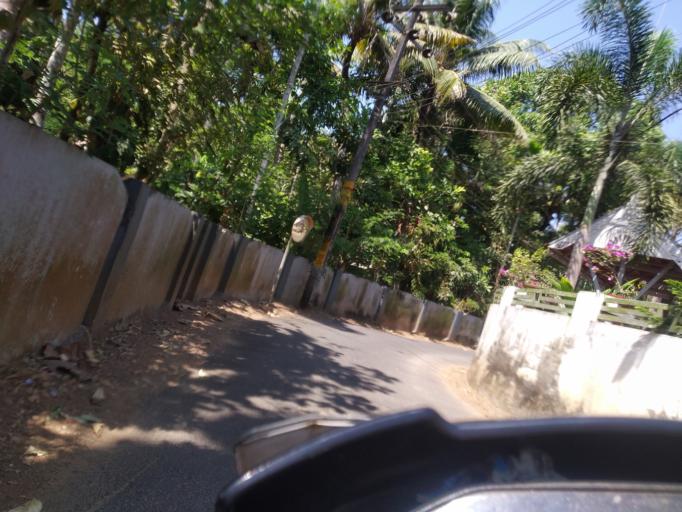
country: IN
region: Kerala
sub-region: Thrissur District
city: Kodungallur
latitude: 10.1803
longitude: 76.2150
